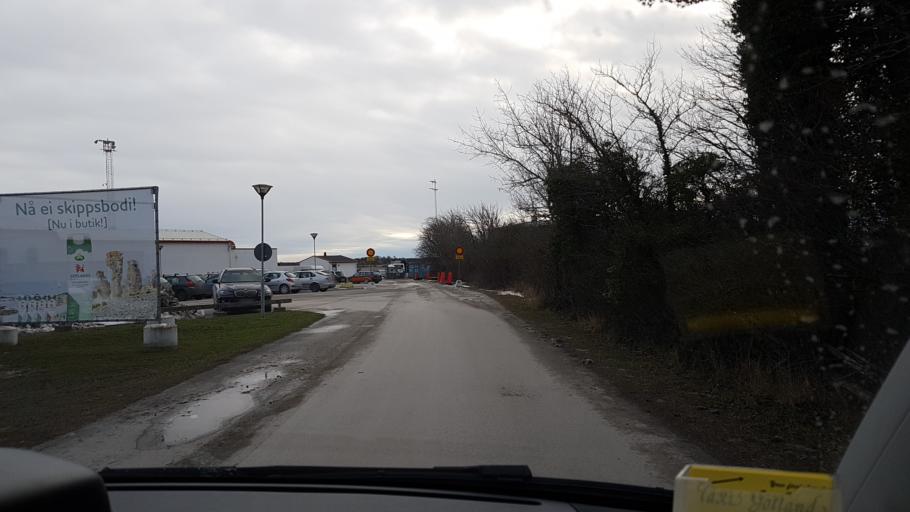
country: SE
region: Gotland
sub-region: Gotland
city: Visby
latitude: 57.6603
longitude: 18.3372
